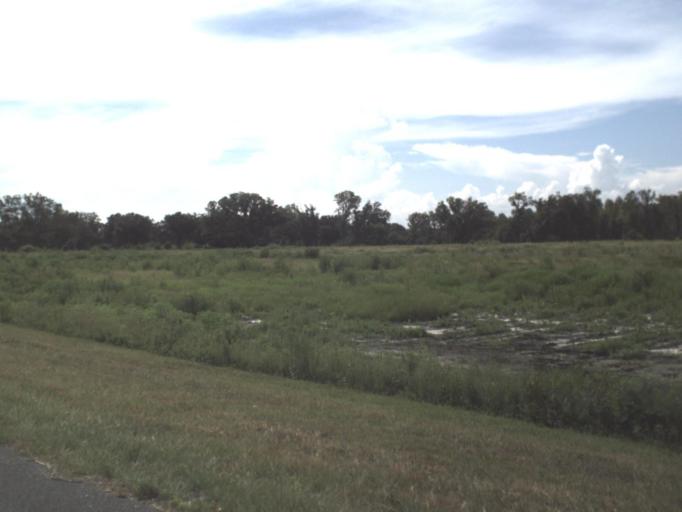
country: US
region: Florida
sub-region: Taylor County
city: Perry
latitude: 30.0811
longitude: -83.5143
